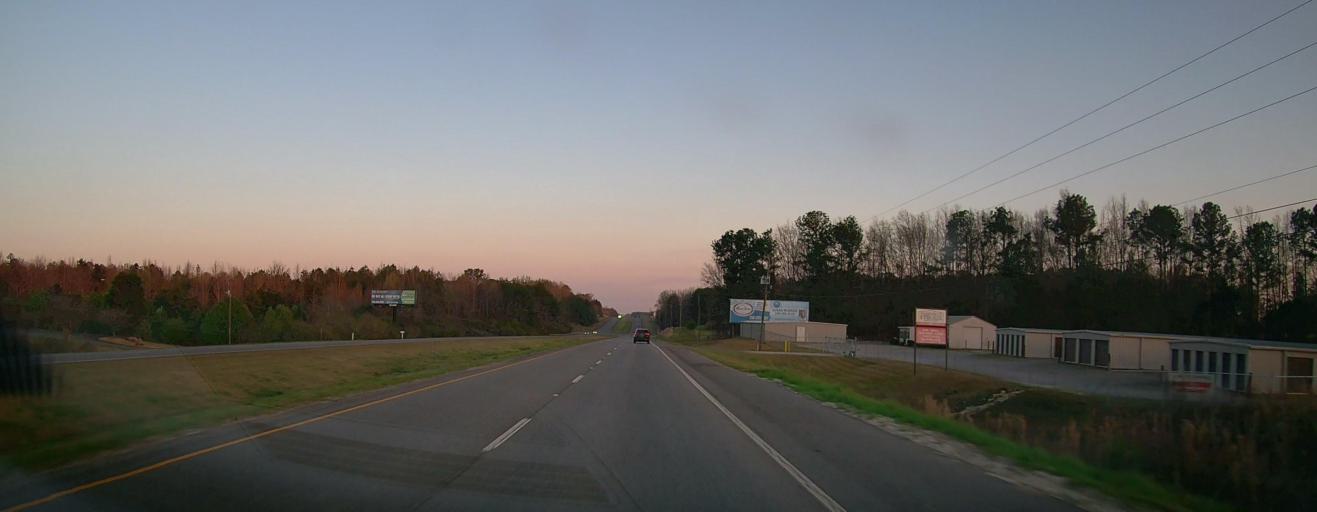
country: US
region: Alabama
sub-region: Tallapoosa County
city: Alexander City
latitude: 32.9617
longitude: -86.0035
